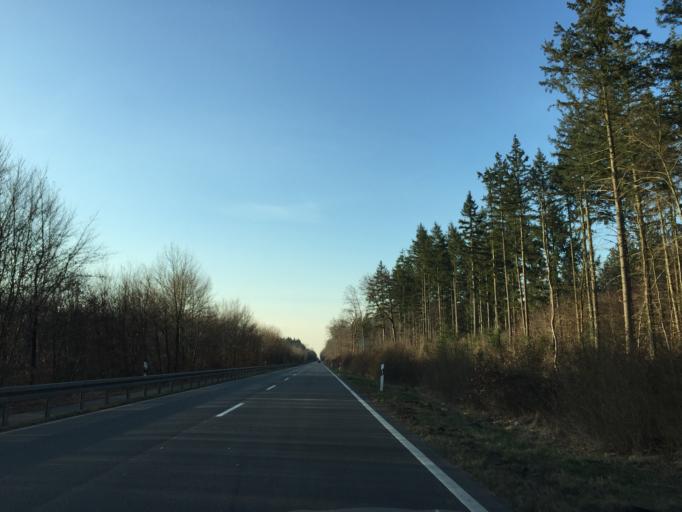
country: DE
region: Baden-Wuerttemberg
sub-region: Karlsruhe Region
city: Walldorf
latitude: 49.3284
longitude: 8.6208
